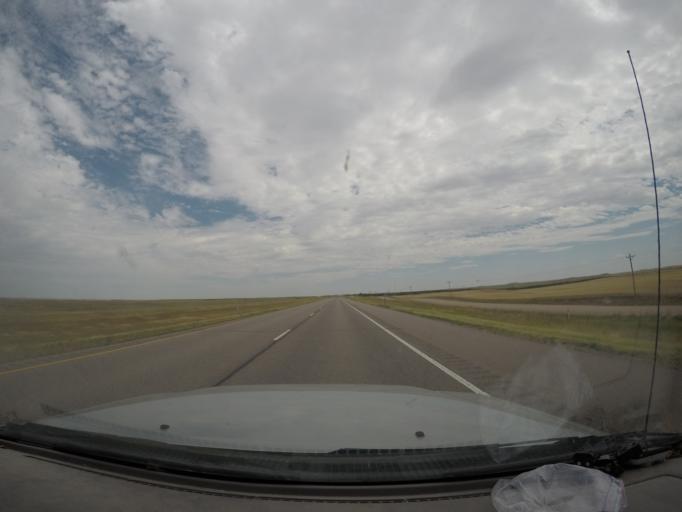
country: US
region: Nebraska
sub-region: Kimball County
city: Kimball
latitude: 41.1918
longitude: -103.7862
